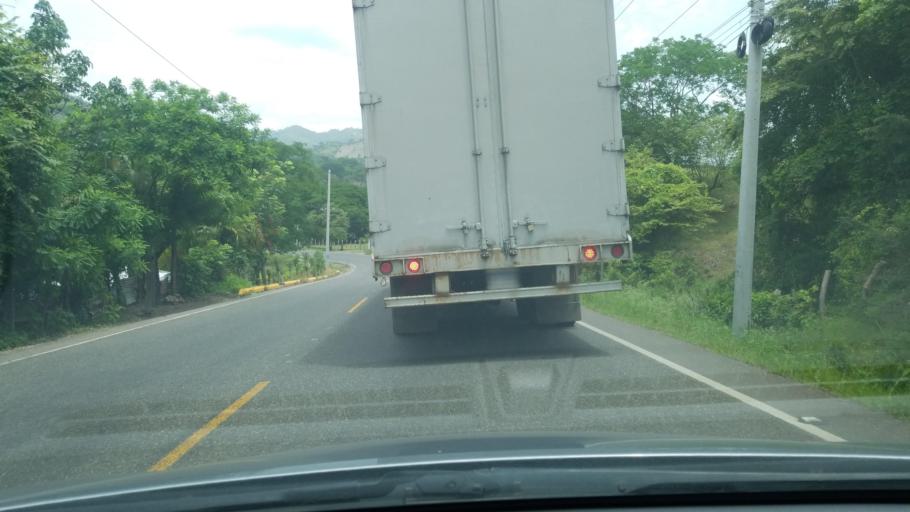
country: HN
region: Copan
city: Ojos de Agua
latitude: 14.7174
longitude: -88.7755
